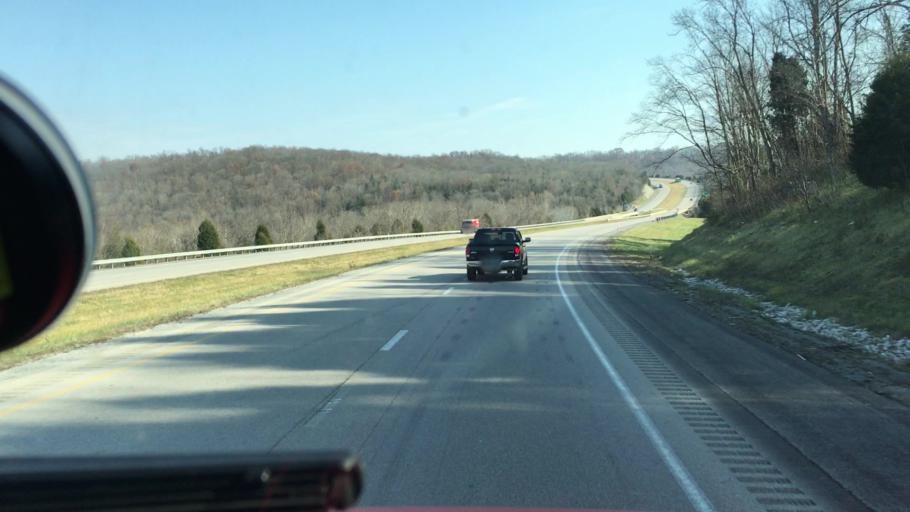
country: US
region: Kentucky
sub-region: Bath County
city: Owingsville
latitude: 38.1242
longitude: -83.7762
